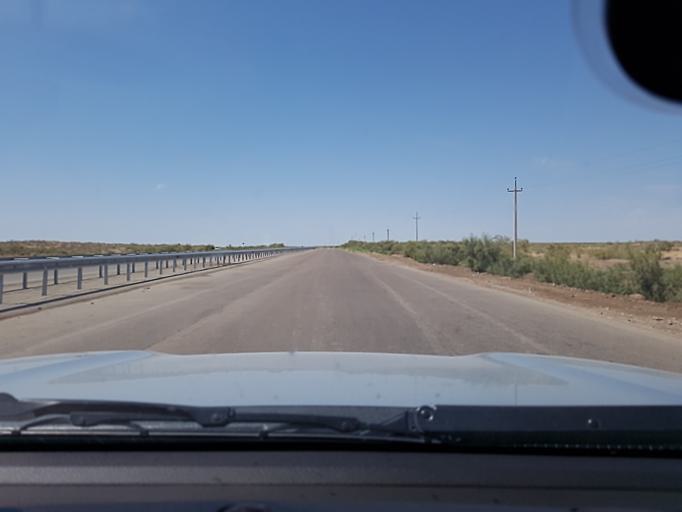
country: TM
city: Akdepe
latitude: 41.7512
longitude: 59.3004
